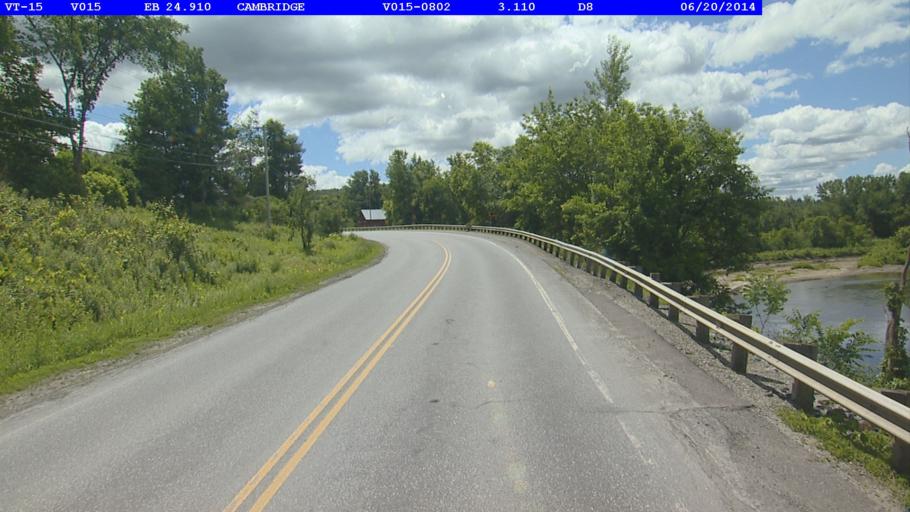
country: US
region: Vermont
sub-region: Lamoille County
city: Johnson
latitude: 44.6470
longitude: -72.8665
